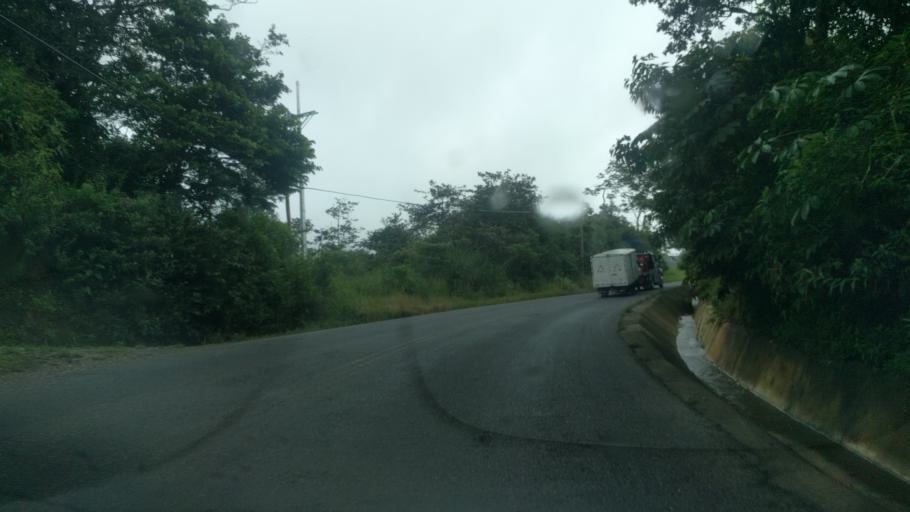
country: CR
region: Alajuela
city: San Rafael
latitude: 10.0353
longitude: -84.5130
